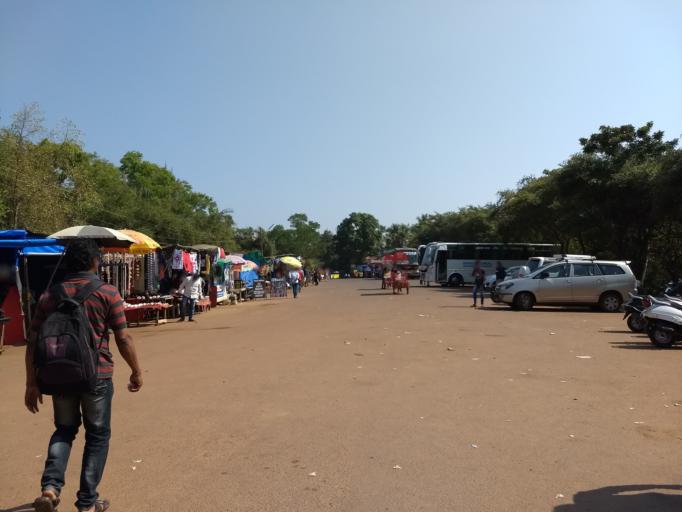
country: IN
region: Goa
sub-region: North Goa
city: Vagator
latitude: 15.5998
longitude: 73.7347
